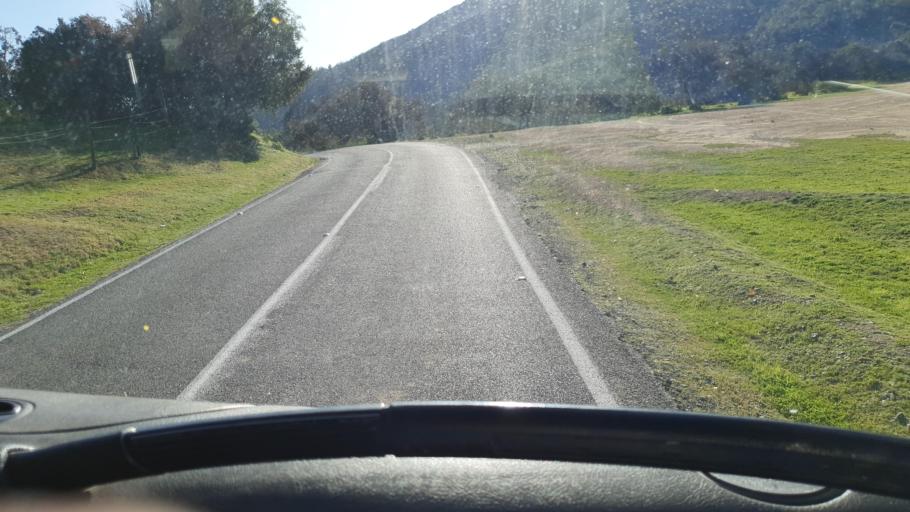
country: CL
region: Valparaiso
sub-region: Provincia de Marga Marga
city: Limache
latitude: -33.1979
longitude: -71.2303
